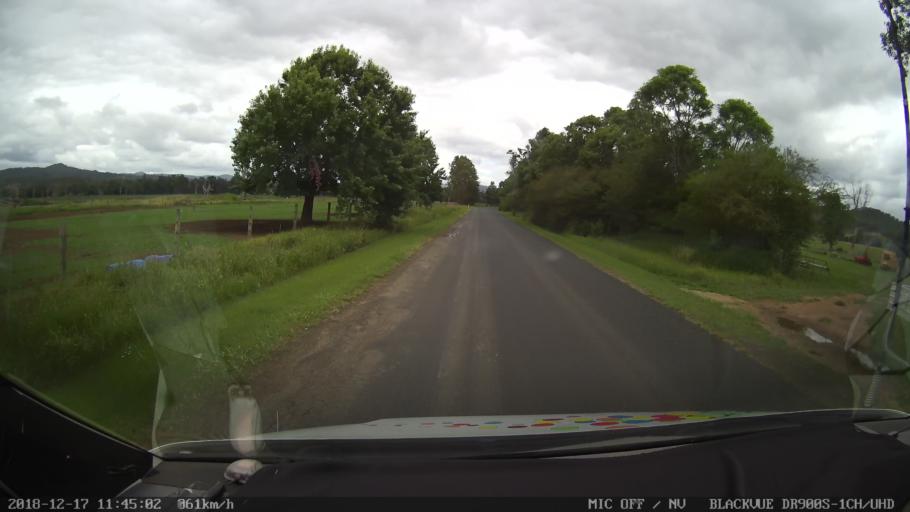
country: AU
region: New South Wales
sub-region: Kyogle
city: Kyogle
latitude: -28.6476
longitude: 152.5949
